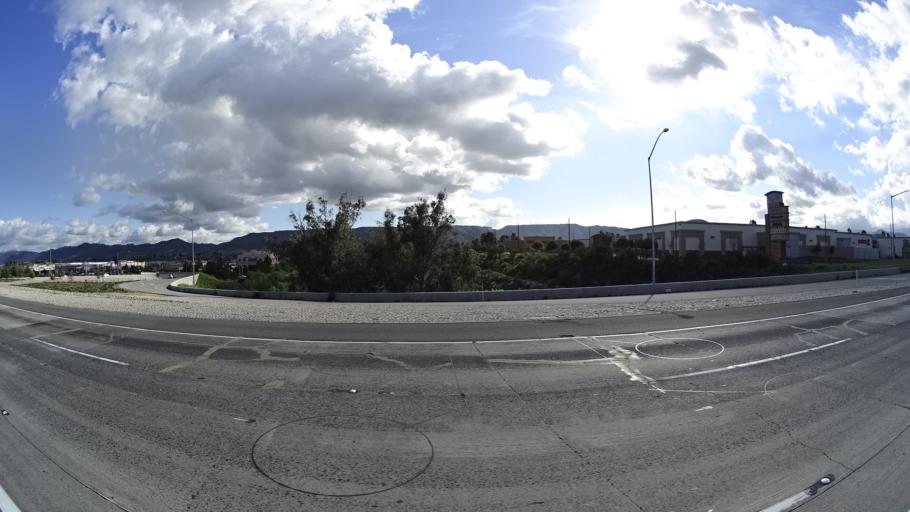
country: US
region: California
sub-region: Riverside County
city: Murrieta
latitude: 33.5669
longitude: -117.2091
